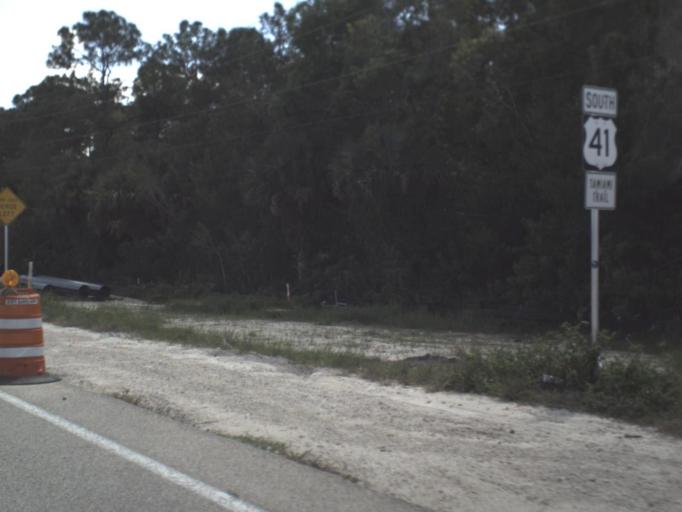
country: US
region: Florida
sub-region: Collier County
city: Lely Resort
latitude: 26.0625
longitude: -81.6982
